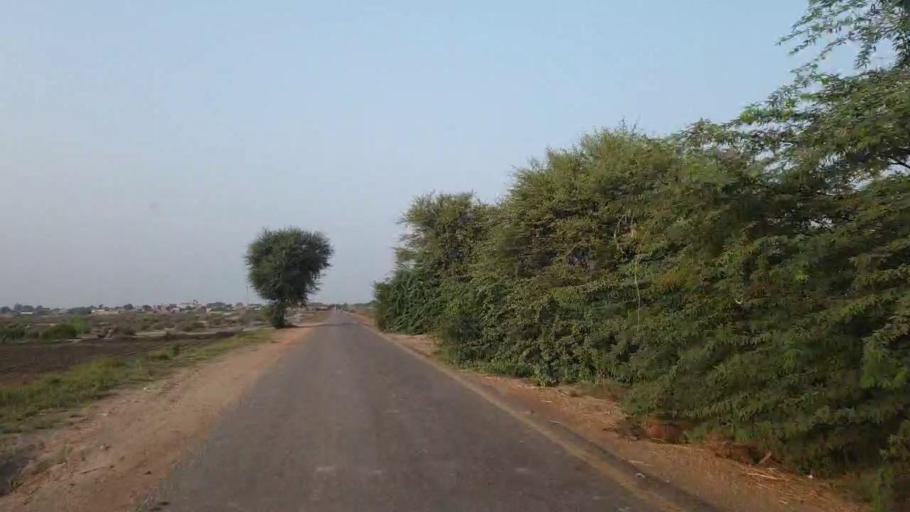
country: PK
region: Sindh
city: Tando Ghulam Ali
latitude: 25.1360
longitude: 68.9587
